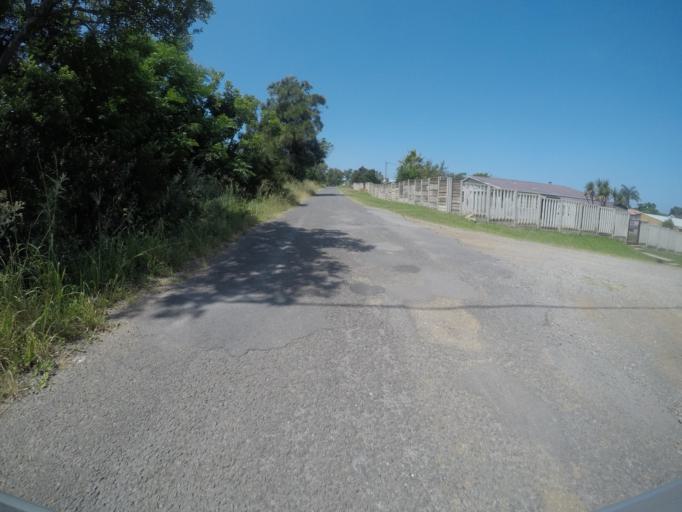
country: ZA
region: Eastern Cape
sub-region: Buffalo City Metropolitan Municipality
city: East London
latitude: -32.9688
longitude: 27.8553
